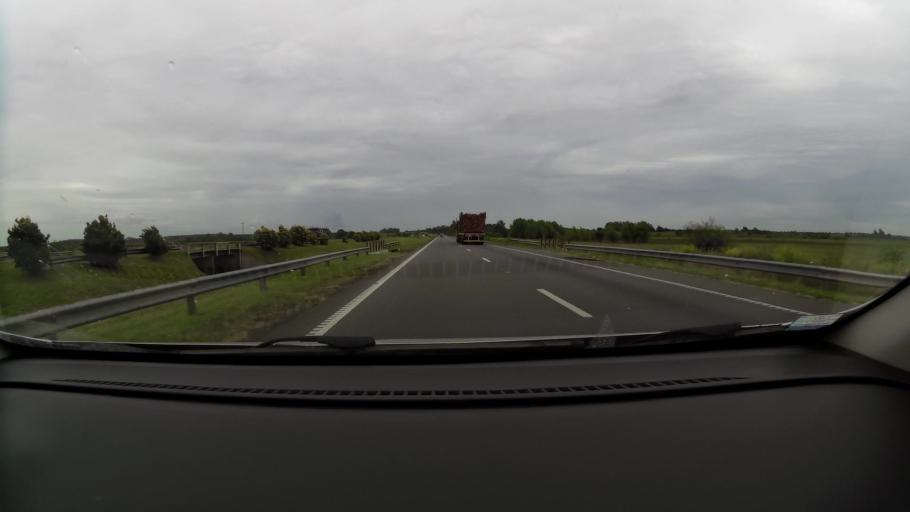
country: AR
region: Buenos Aires
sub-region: Partido de Baradero
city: Baradero
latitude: -33.9579
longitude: -59.3950
